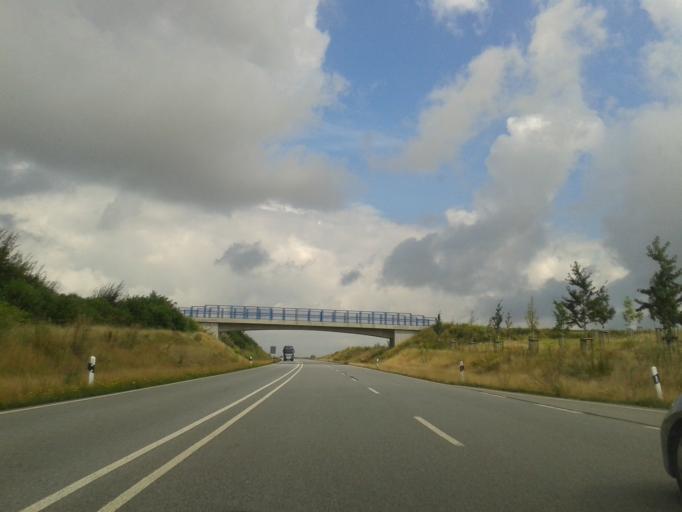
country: DE
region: Saxony
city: Radeberg
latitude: 51.0822
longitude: 13.9376
